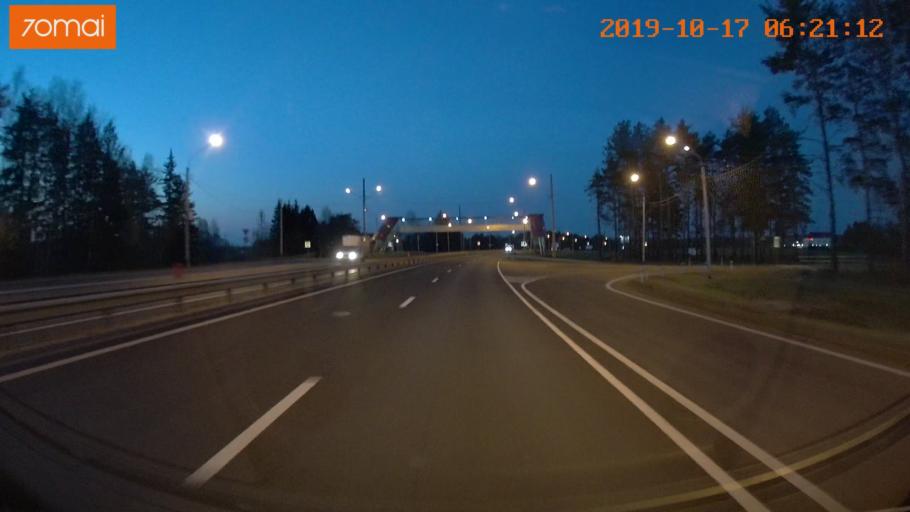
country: RU
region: Ivanovo
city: Lezhnevo
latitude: 56.8050
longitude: 40.8870
